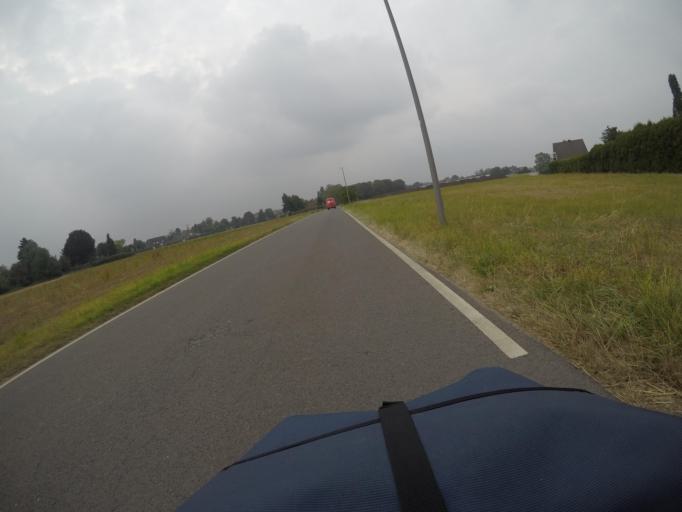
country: DE
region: North Rhine-Westphalia
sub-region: Regierungsbezirk Dusseldorf
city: Krefeld
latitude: 51.2984
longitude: 6.6125
